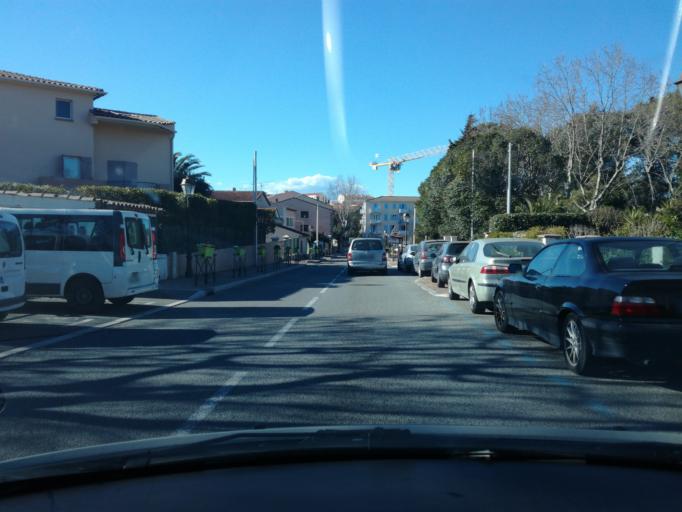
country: FR
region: Provence-Alpes-Cote d'Azur
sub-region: Departement du Var
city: Puget-sur-Argens
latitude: 43.4534
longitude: 6.6898
